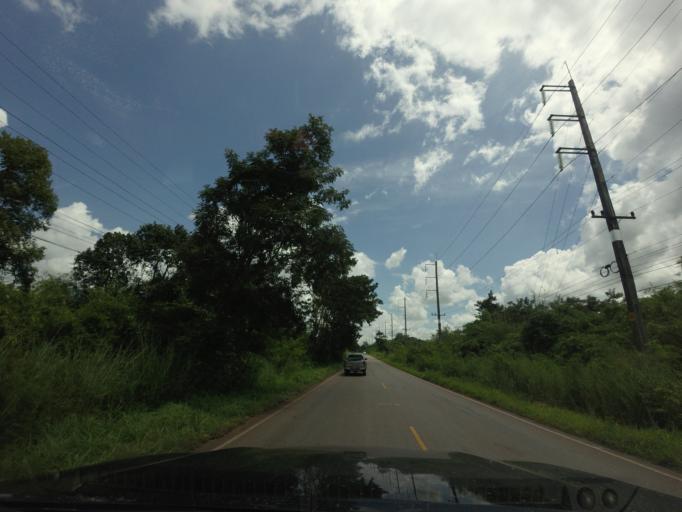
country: TH
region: Nong Khai
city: Sa Khrai
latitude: 17.5743
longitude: 102.6465
